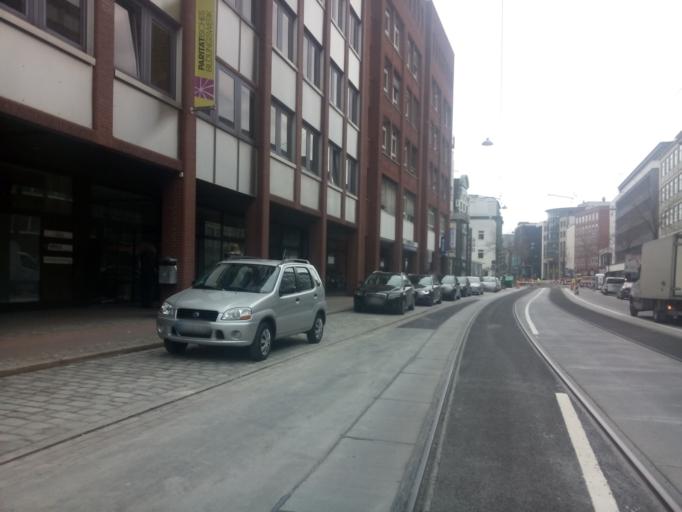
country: DE
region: Bremen
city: Bremen
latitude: 53.0804
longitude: 8.7978
